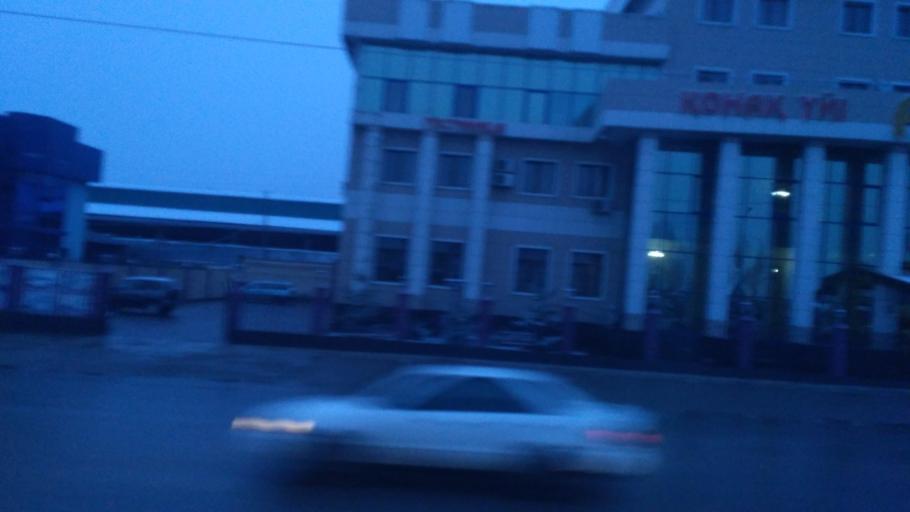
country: KZ
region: Ongtustik Qazaqstan
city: Shymkent
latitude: 42.3543
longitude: 69.5271
